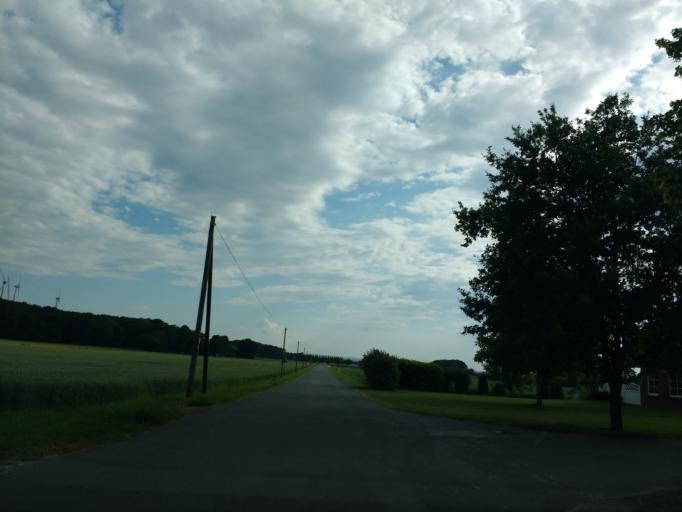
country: DE
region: North Rhine-Westphalia
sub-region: Regierungsbezirk Detmold
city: Salzkotten
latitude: 51.7118
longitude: 8.6479
